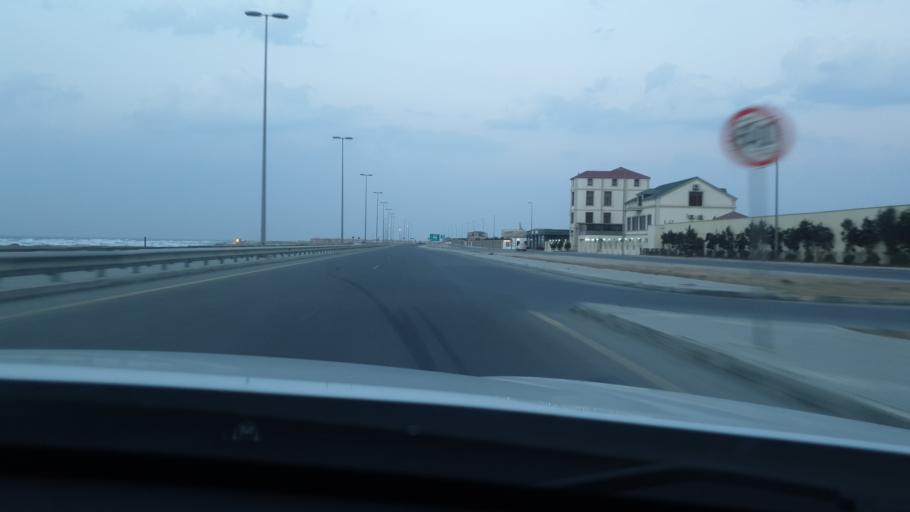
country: AZ
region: Baki
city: Bilajer
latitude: 40.5879
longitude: 50.0450
